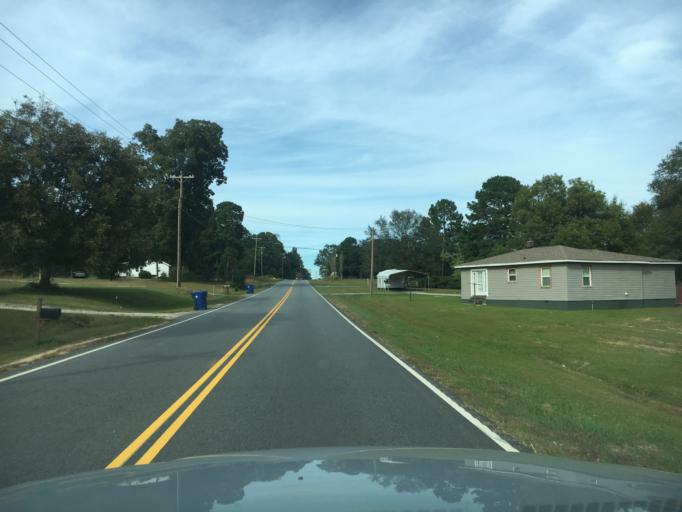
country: US
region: South Carolina
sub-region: Spartanburg County
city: Duncan
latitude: 34.9131
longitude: -82.1450
